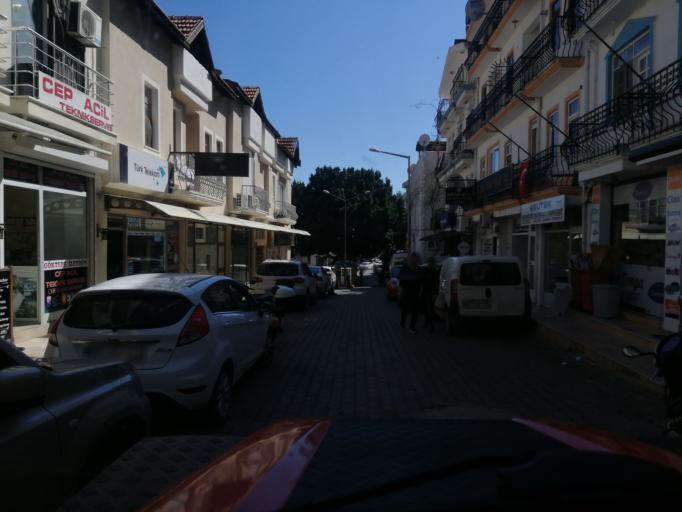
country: TR
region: Antalya
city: Kas
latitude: 36.2010
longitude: 29.6395
